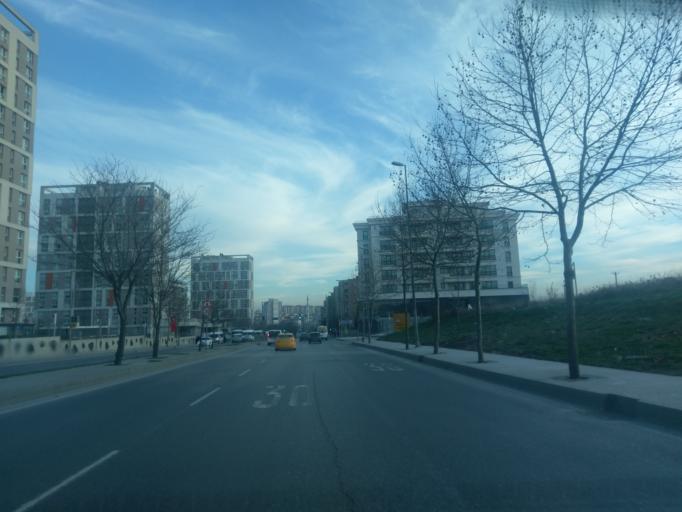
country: TR
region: Istanbul
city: Mahmutbey
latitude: 41.0399
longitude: 28.7609
